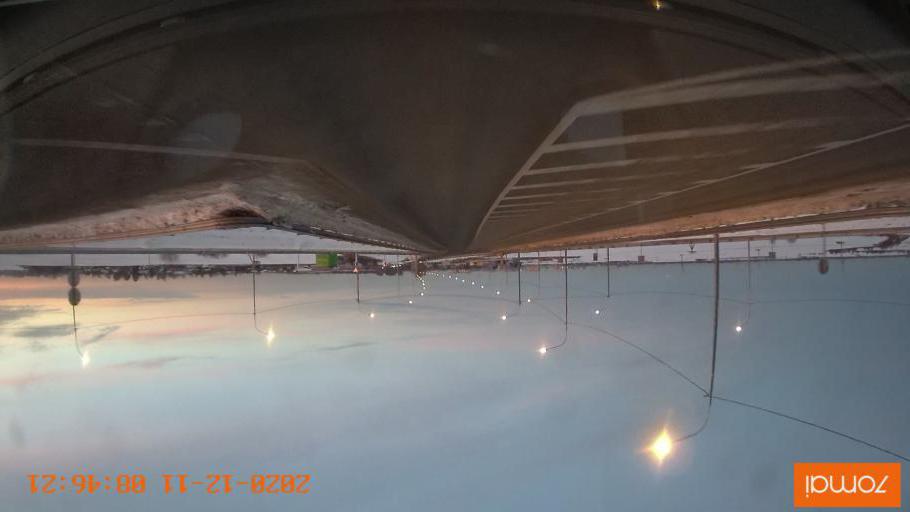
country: RU
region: Vologda
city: Vologda
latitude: 59.1576
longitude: 39.8140
